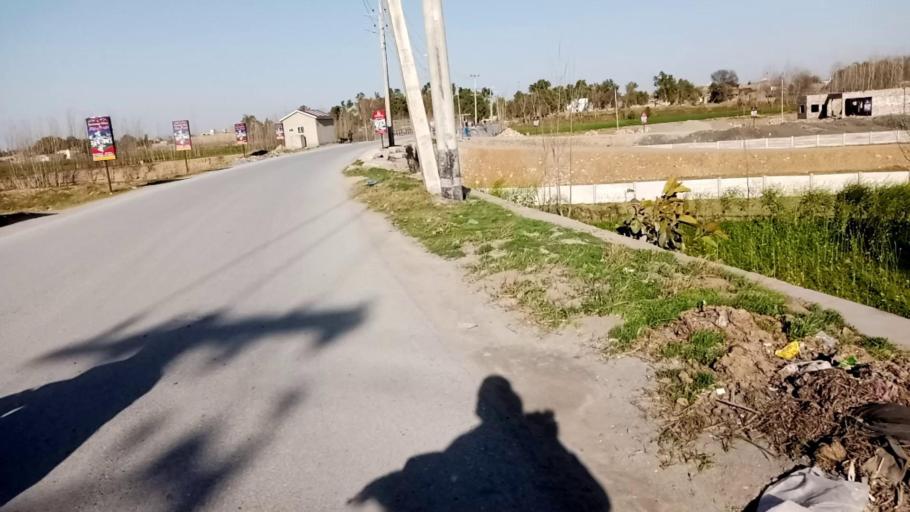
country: PK
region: Khyber Pakhtunkhwa
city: Peshawar
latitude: 34.0510
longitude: 71.5271
